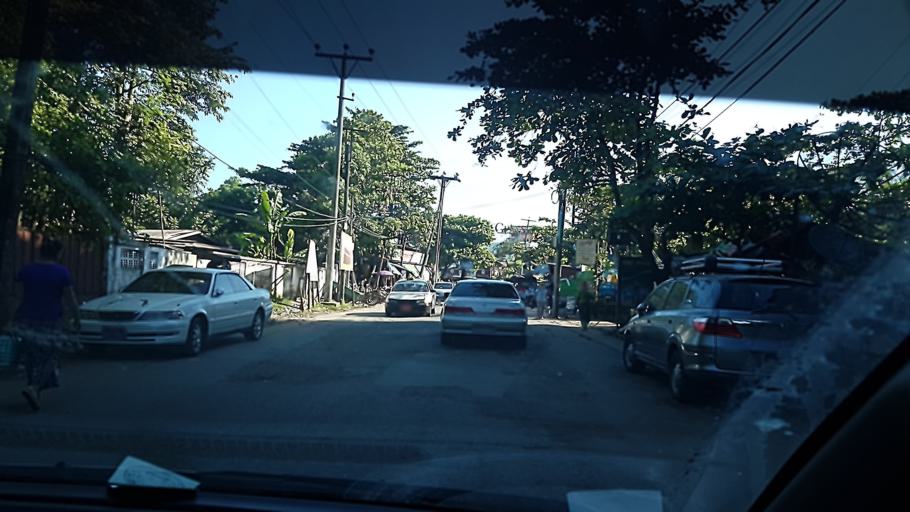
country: MM
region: Yangon
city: Yangon
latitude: 16.8544
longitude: 96.1158
